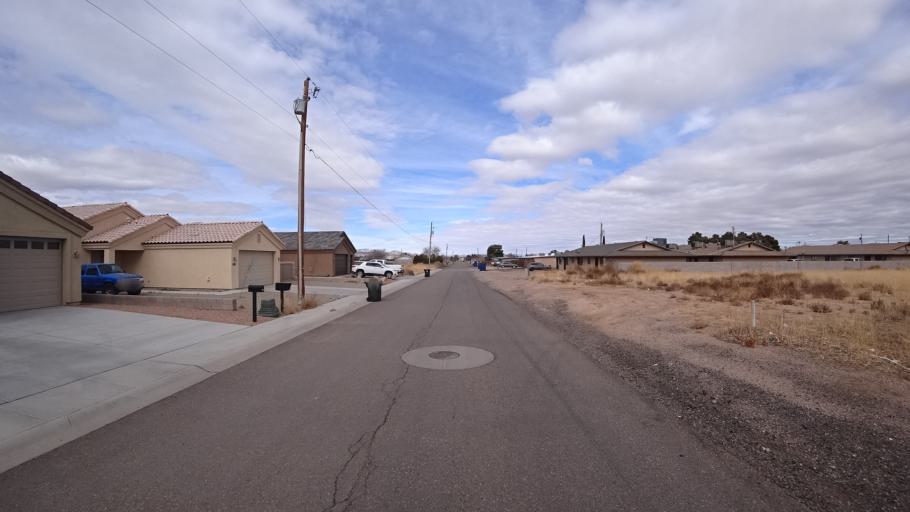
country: US
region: Arizona
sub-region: Mohave County
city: New Kingman-Butler
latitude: 35.2342
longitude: -114.0200
